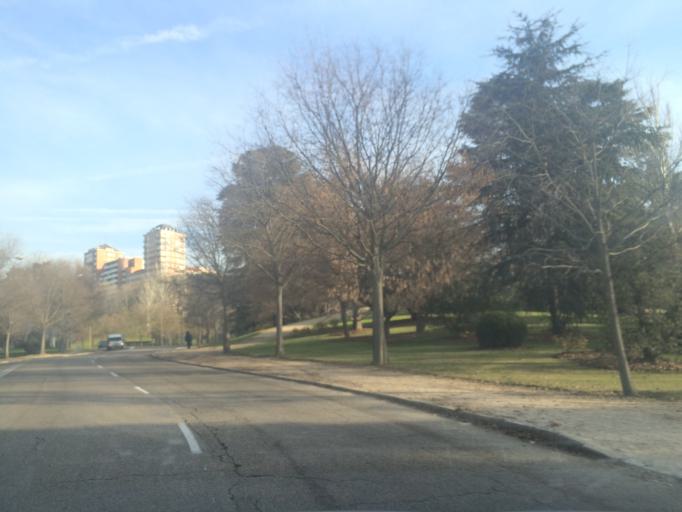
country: ES
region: Madrid
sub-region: Provincia de Madrid
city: Moncloa-Aravaca
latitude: 40.4327
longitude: -3.7290
